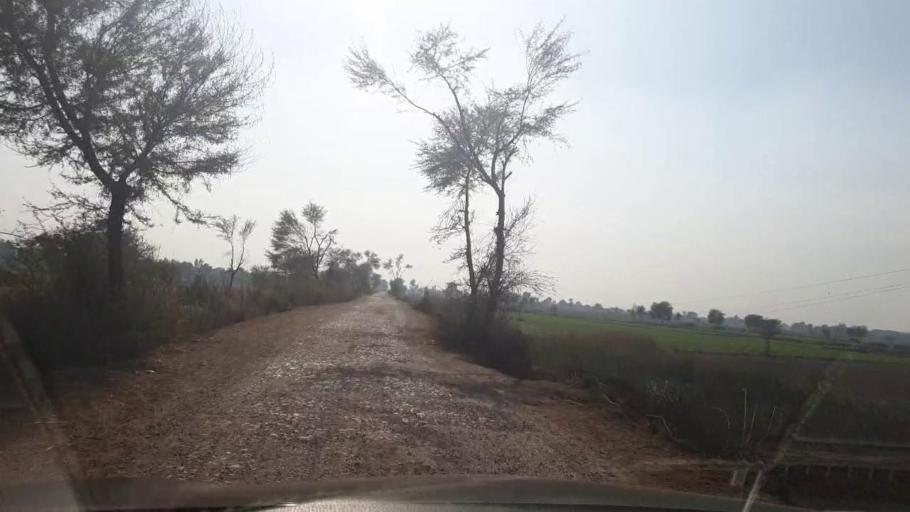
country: PK
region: Sindh
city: Khairpur
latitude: 28.1257
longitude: 69.6440
